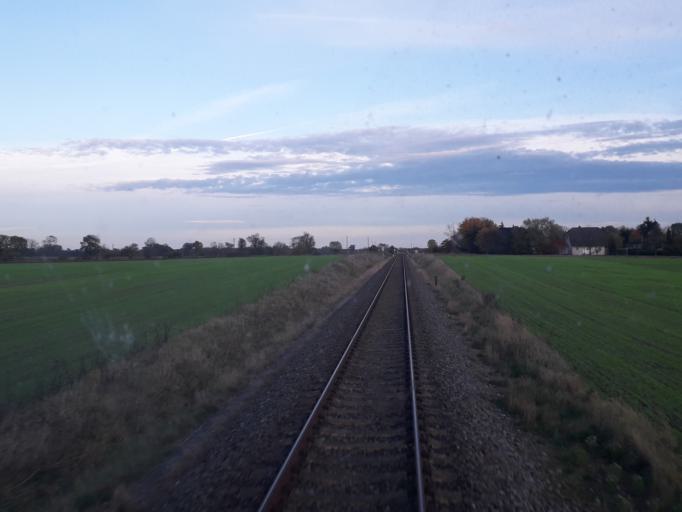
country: DE
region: Brandenburg
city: Dabergotz
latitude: 52.9341
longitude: 12.7409
